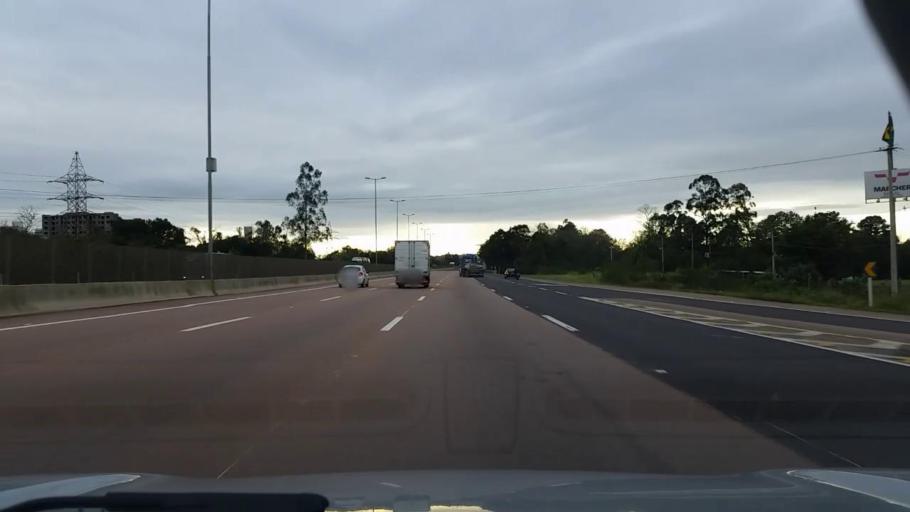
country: BR
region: Rio Grande do Sul
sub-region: Gravatai
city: Gravatai
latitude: -29.9544
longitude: -51.0016
